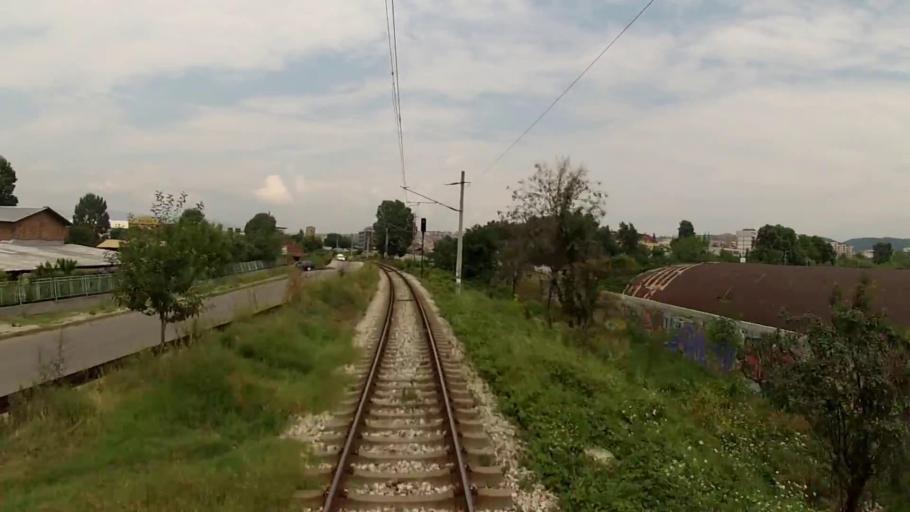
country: BG
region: Blagoevgrad
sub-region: Obshtina Blagoevgrad
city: Blagoevgrad
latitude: 41.9989
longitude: 23.0884
